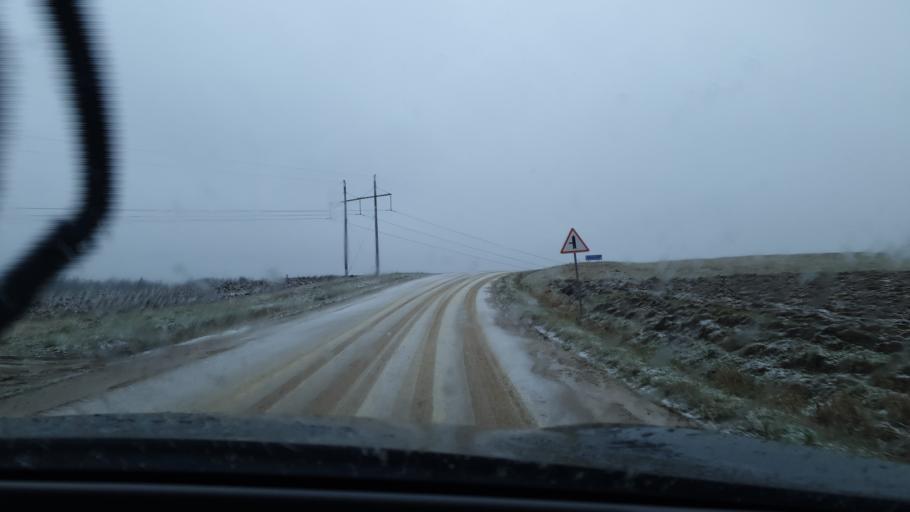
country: LT
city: Jieznas
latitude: 54.5521
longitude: 24.3141
